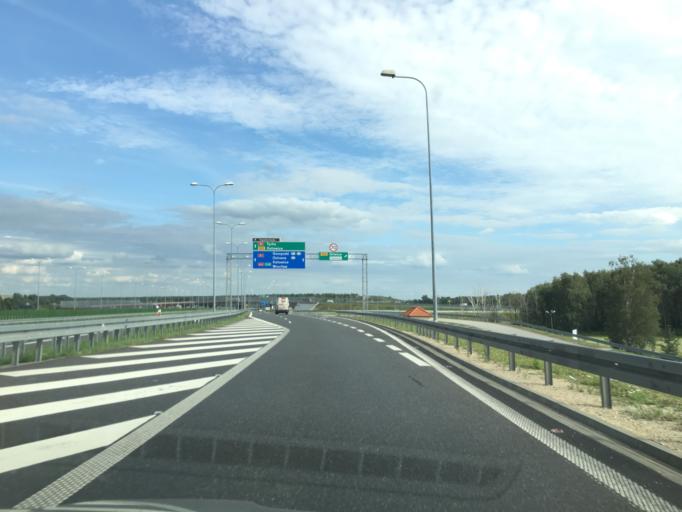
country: PL
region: Silesian Voivodeship
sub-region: Powiat gliwicki
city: Przyszowice
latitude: 50.2830
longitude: 18.7190
